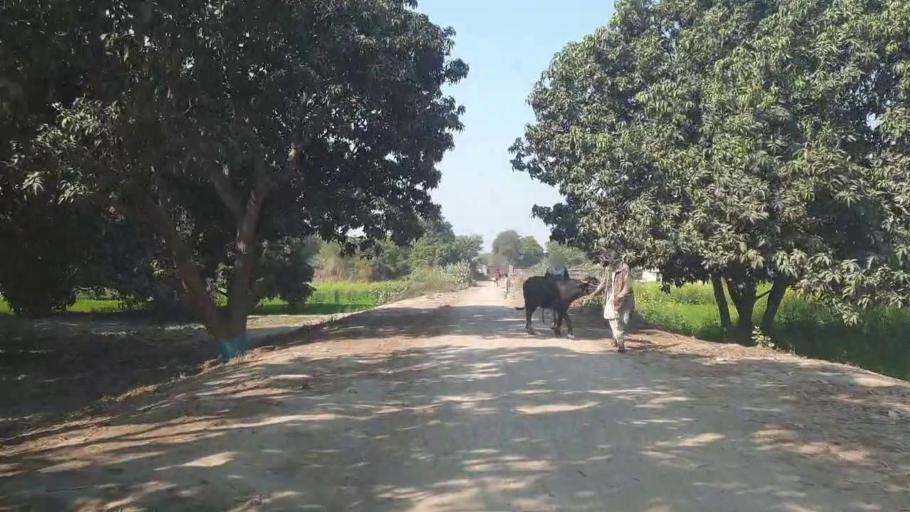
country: PK
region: Sindh
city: Tando Allahyar
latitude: 25.4707
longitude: 68.7784
